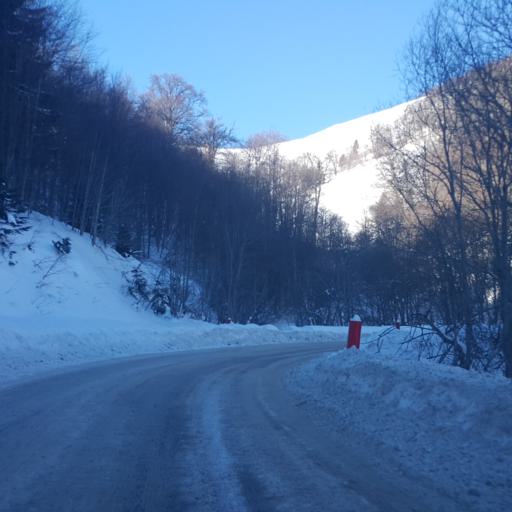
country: XK
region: Mitrovica
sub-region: Komuna e Leposaviqit
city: Leposaviq
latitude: 43.3166
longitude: 20.8445
